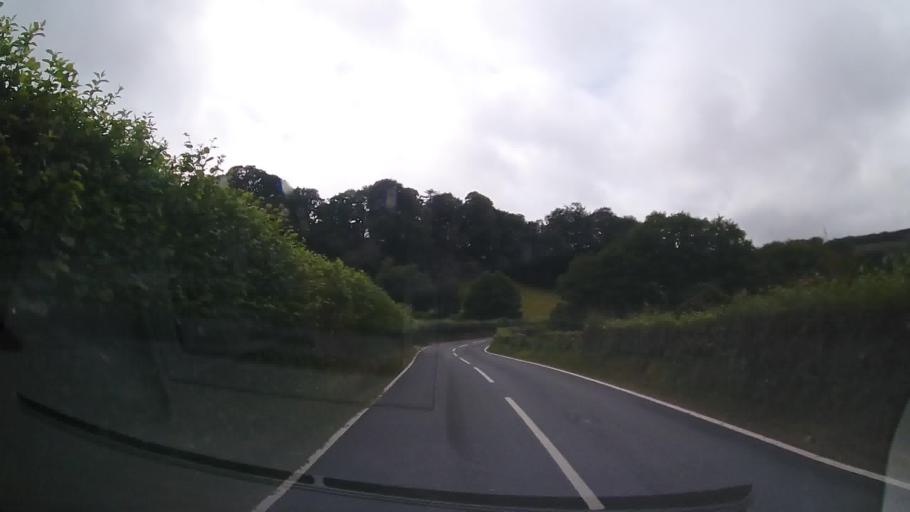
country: GB
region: Wales
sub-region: Denbighshire
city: Llandrillo
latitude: 52.9163
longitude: -3.5059
